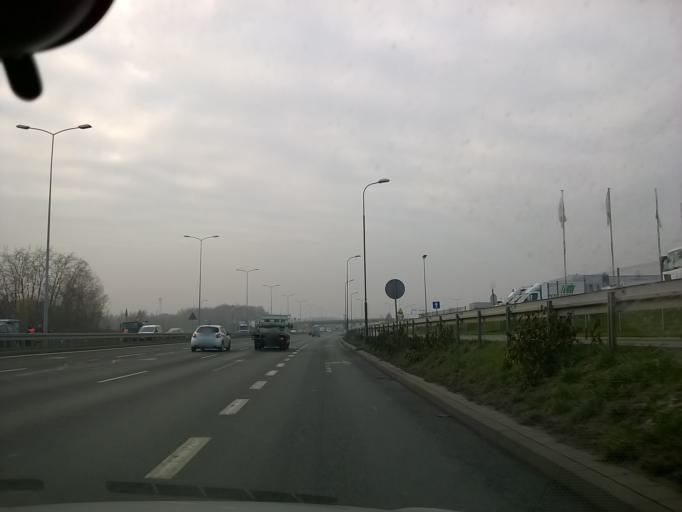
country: PL
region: Silesian Voivodeship
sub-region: Ruda Slaska
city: Ruda Slaska
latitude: 50.2996
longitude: 18.8644
